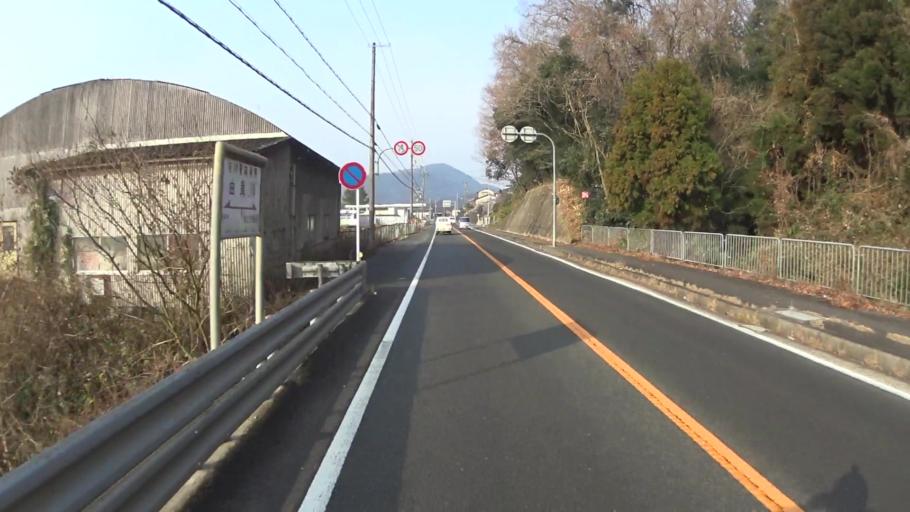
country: JP
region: Kyoto
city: Ayabe
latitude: 35.2910
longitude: 135.2760
